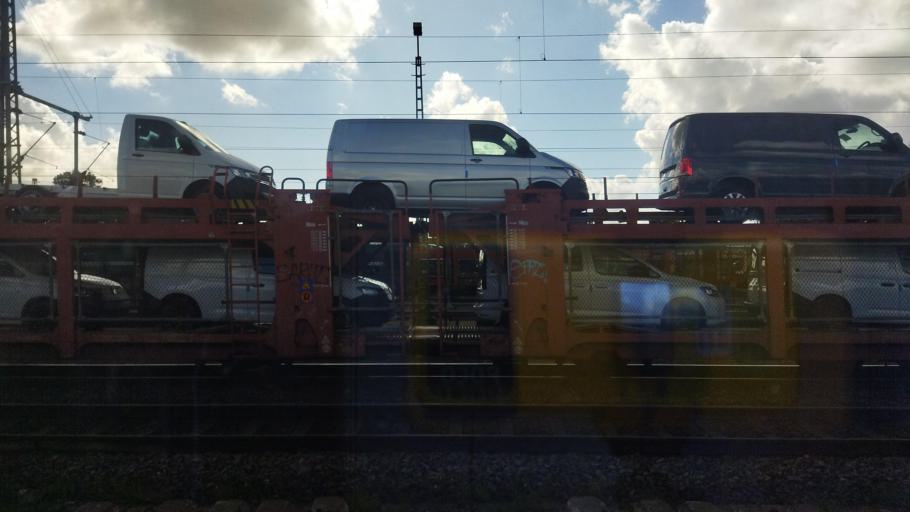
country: DE
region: Lower Saxony
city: Emden
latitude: 53.3596
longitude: 7.2087
